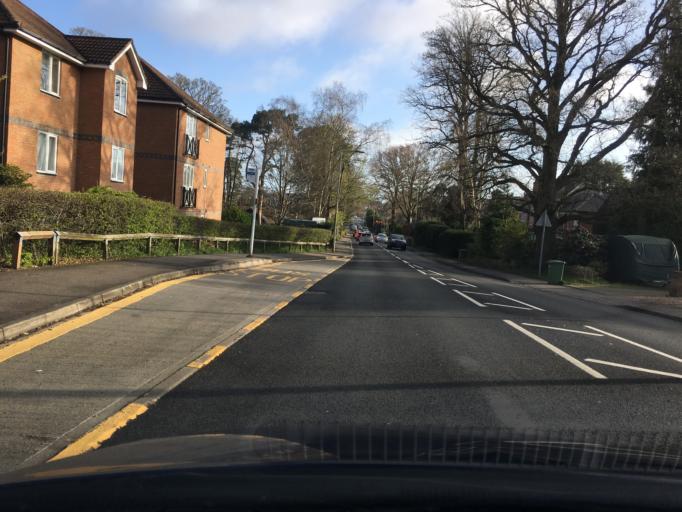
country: GB
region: England
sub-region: Bracknell Forest
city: Crowthorne
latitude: 51.3637
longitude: -0.7971
